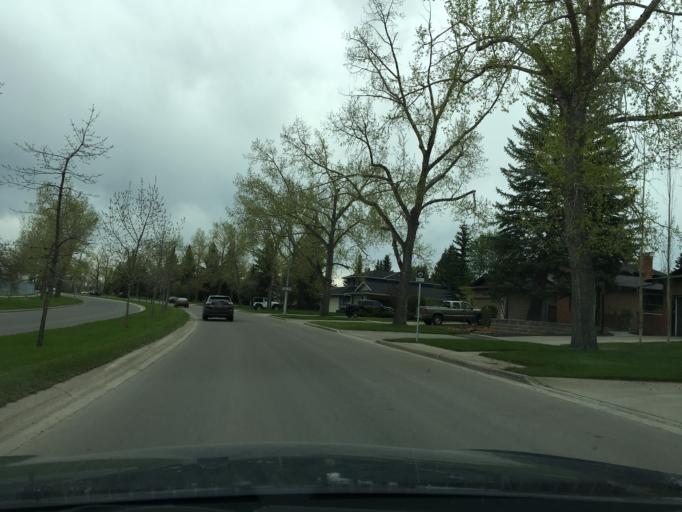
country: CA
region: Alberta
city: Calgary
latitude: 50.9438
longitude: -114.0607
